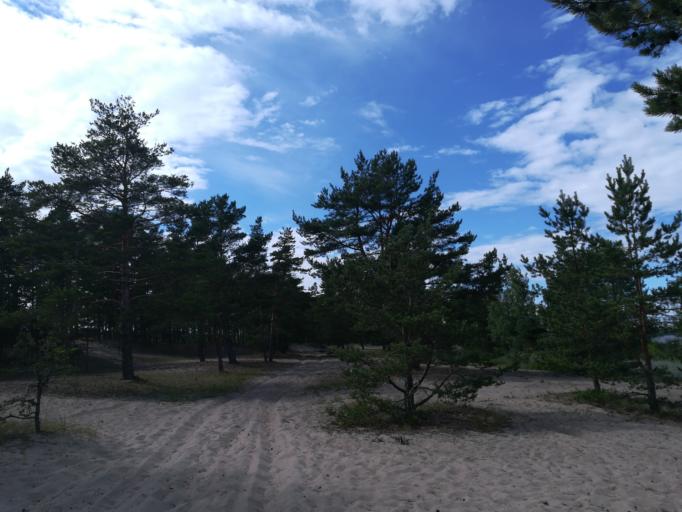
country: RU
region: Leningrad
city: Ust'-Luga
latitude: 59.6814
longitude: 28.2312
